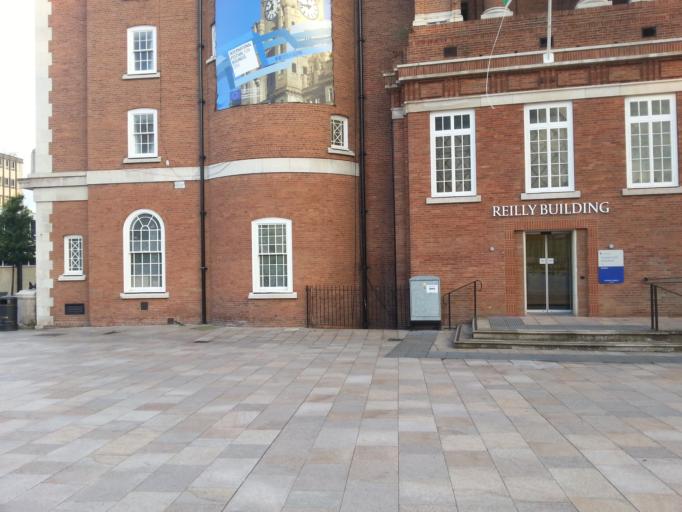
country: GB
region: England
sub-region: Liverpool
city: Liverpool
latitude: 53.4058
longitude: -2.9657
